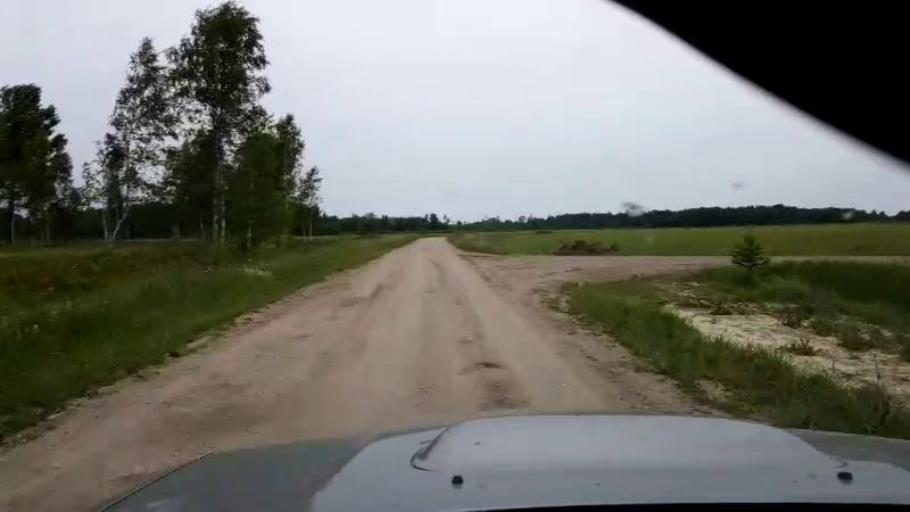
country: EE
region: Paernumaa
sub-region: Halinga vald
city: Parnu-Jaagupi
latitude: 58.5431
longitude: 24.6091
